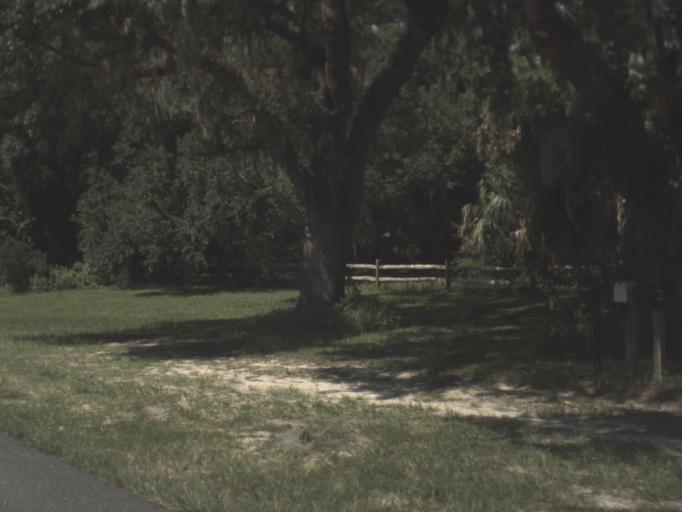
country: US
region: Florida
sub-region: Levy County
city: Inglis
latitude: 28.9659
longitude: -82.6333
